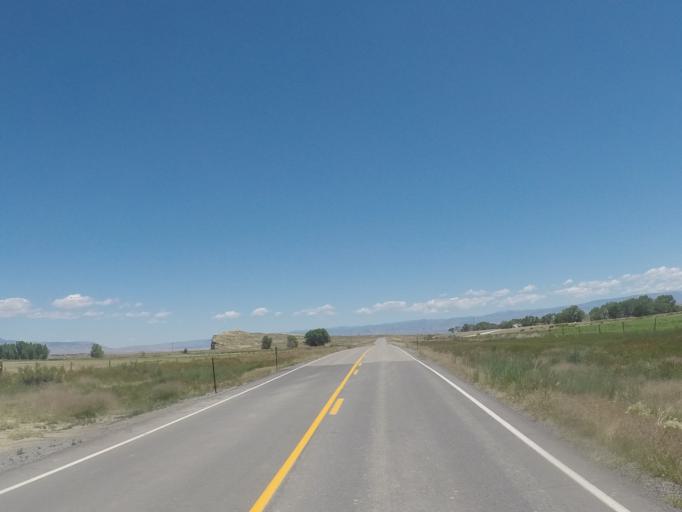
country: US
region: Wyoming
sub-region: Big Horn County
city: Lovell
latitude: 44.7786
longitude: -108.4944
